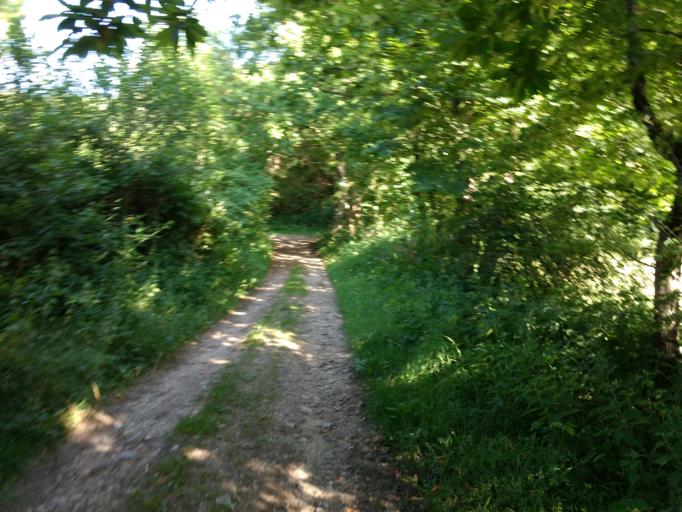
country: FR
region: Midi-Pyrenees
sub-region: Departement de l'Aveyron
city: La Loubiere
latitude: 44.3601
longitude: 2.6911
